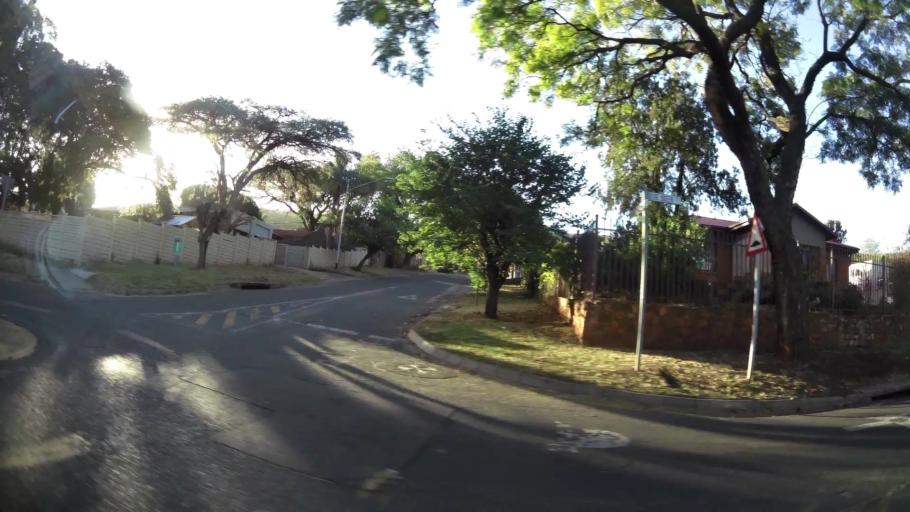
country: ZA
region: Gauteng
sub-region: City of Tshwane Metropolitan Municipality
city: Pretoria
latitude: -25.6977
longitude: 28.2085
